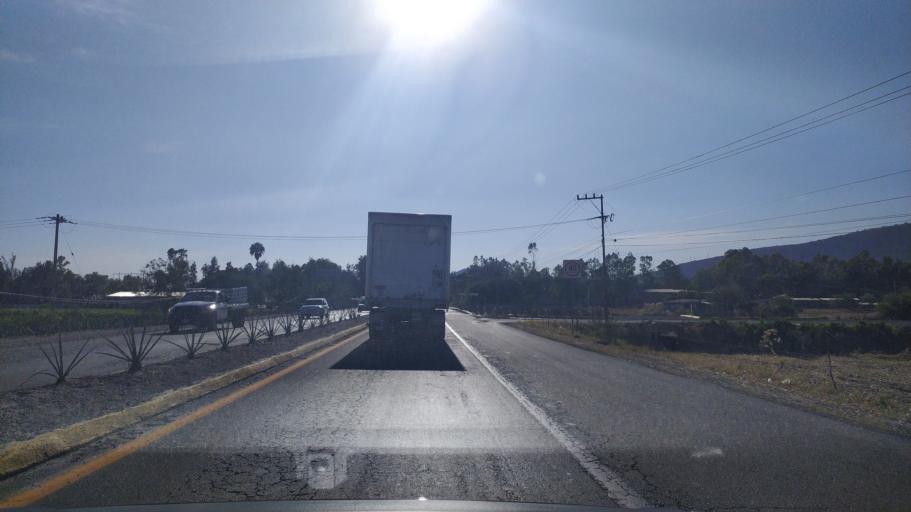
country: MX
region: Jalisco
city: Jamay
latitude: 20.2941
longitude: -102.6719
